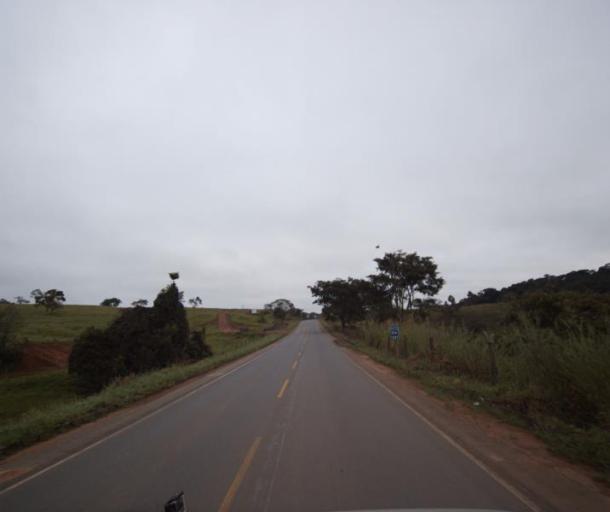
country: BR
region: Goias
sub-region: Pirenopolis
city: Pirenopolis
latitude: -15.9092
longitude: -48.8019
